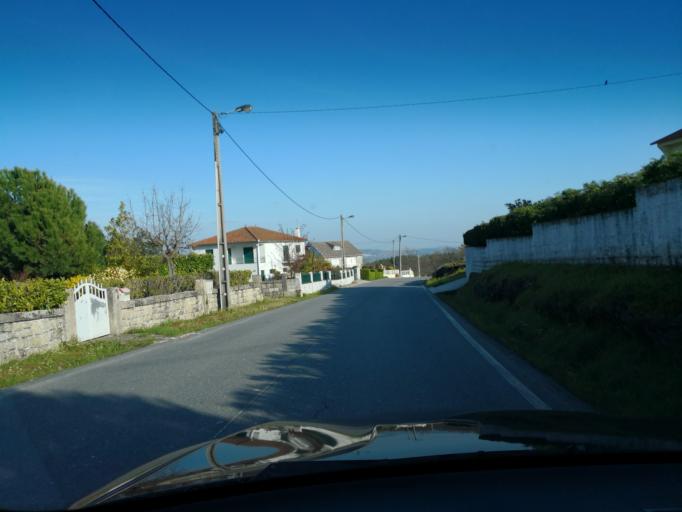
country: PT
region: Vila Real
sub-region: Sabrosa
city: Sabrosa
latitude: 41.3567
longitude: -7.6140
